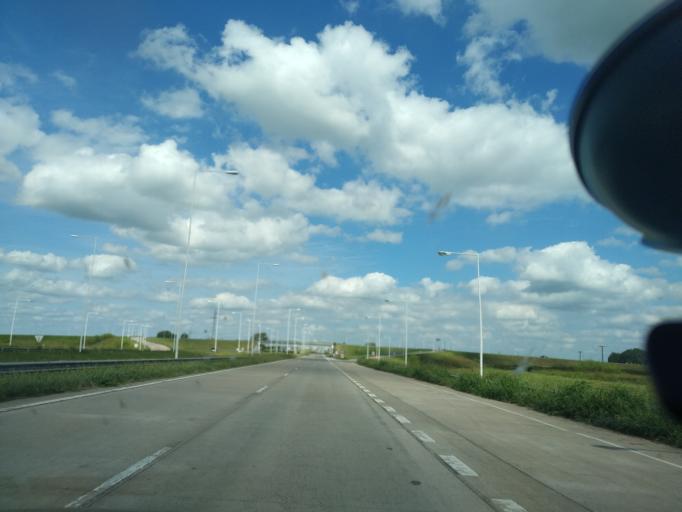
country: AR
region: Santa Fe
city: Canada de Gomez
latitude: -32.8461
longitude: -61.3947
